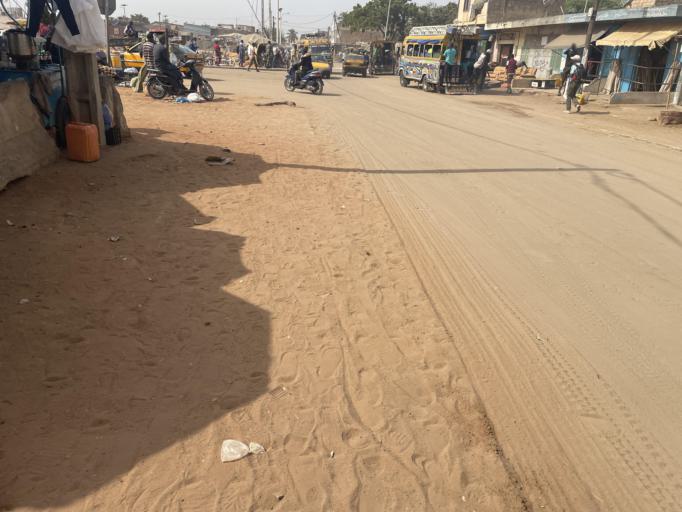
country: SN
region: Dakar
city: Pikine
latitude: 14.7604
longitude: -17.3801
